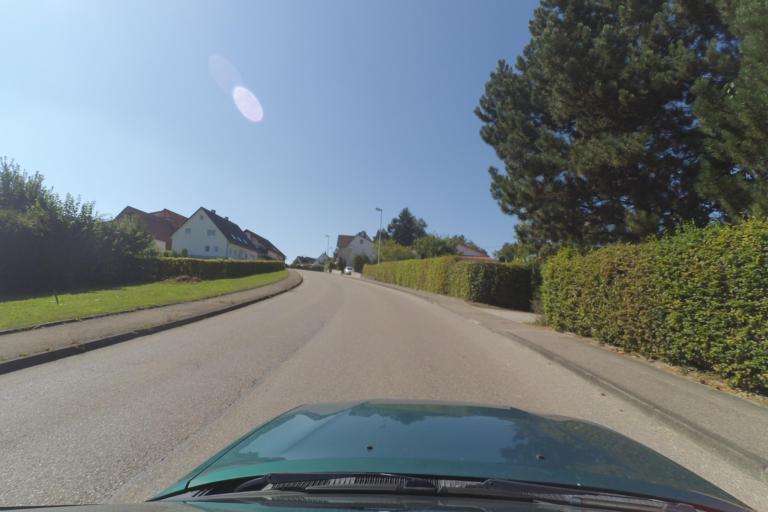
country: DE
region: Baden-Wuerttemberg
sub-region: Regierungsbezirk Stuttgart
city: Steinheim am Albuch
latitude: 48.7293
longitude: 10.0722
